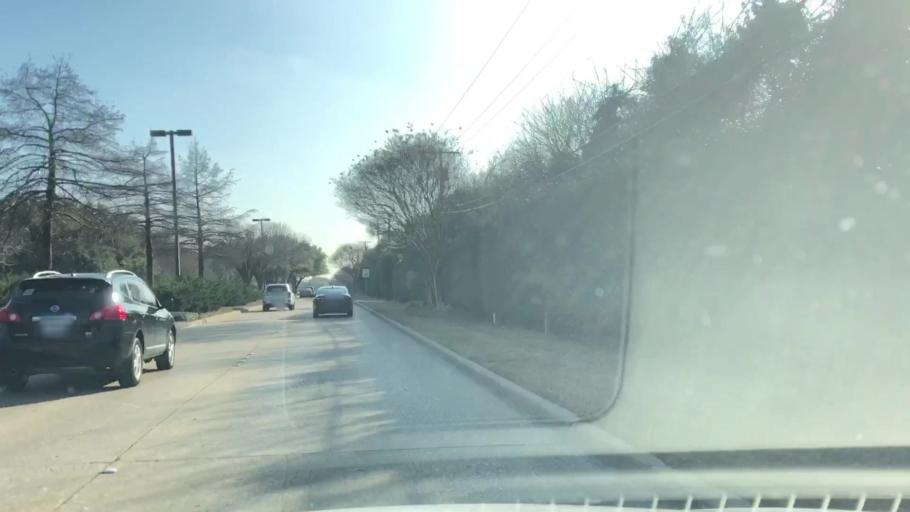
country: US
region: Texas
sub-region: Dallas County
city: Addison
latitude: 32.9450
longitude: -96.8558
